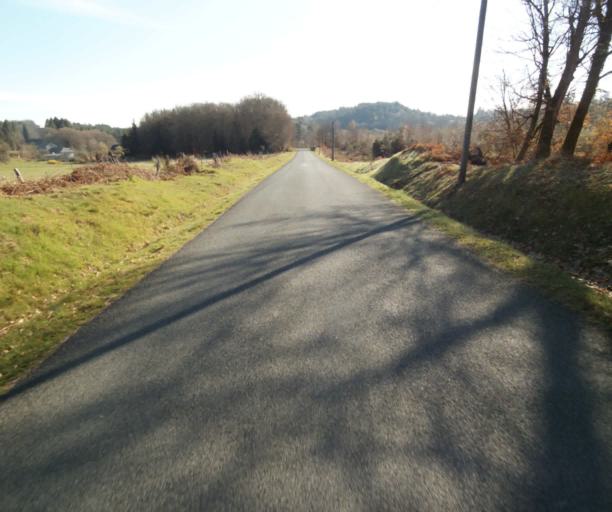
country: FR
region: Limousin
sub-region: Departement de la Correze
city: Correze
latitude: 45.3046
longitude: 1.8750
